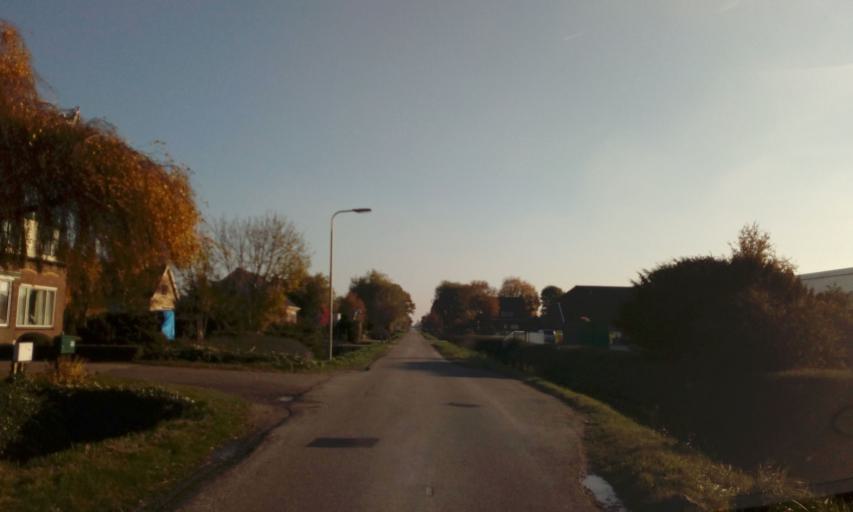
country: NL
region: South Holland
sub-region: Gemeente Lansingerland
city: Bleiswijk
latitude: 52.0126
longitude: 4.5949
